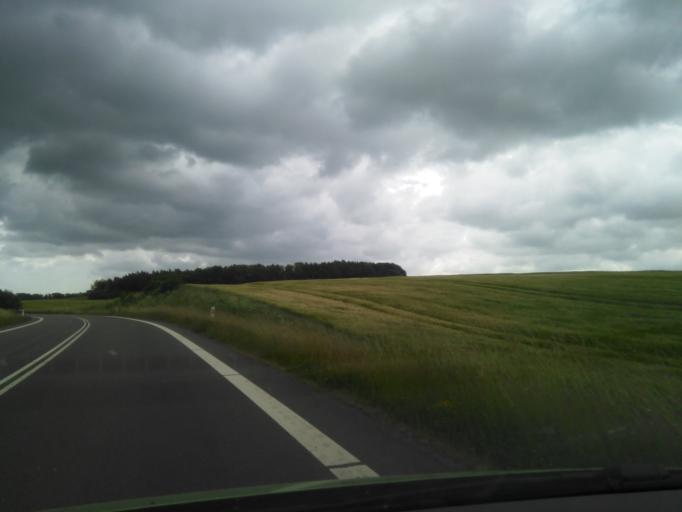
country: DK
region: Capital Region
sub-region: Bornholm Kommune
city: Akirkeby
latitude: 55.2218
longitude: 14.8949
